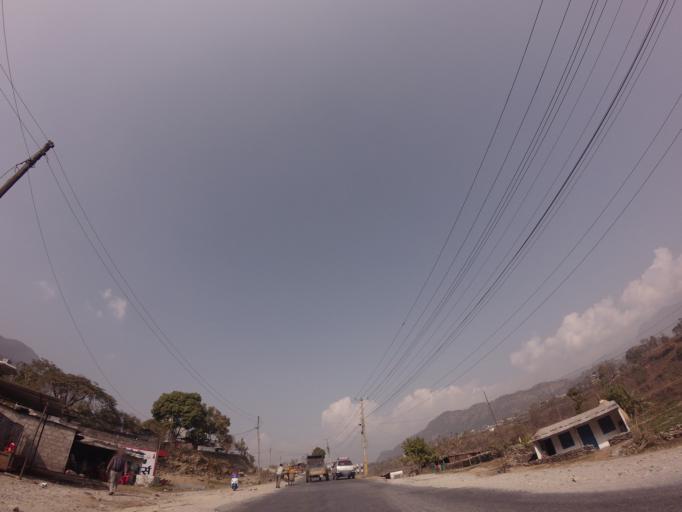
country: NP
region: Western Region
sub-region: Gandaki Zone
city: Pokhara
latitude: 28.2557
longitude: 83.9654
